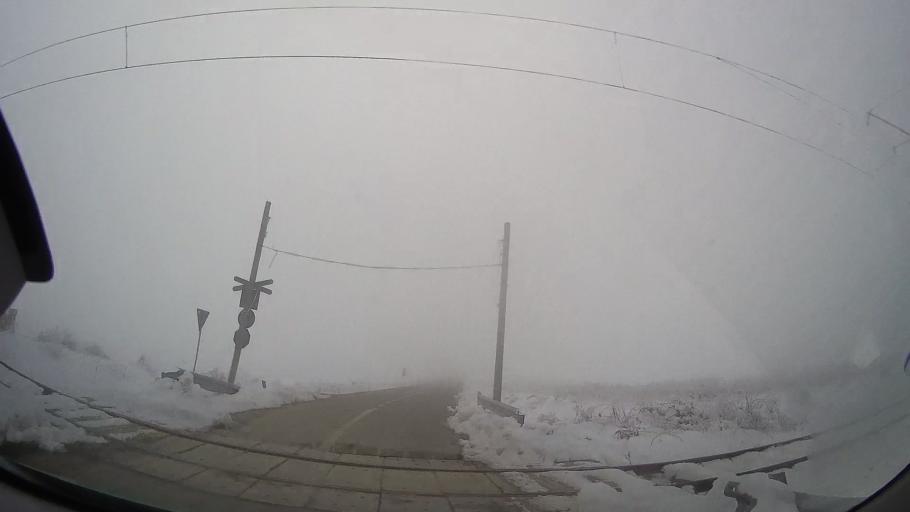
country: RO
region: Iasi
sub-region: Comuna Valea Seaca
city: Topile
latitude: 47.2757
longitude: 26.6709
